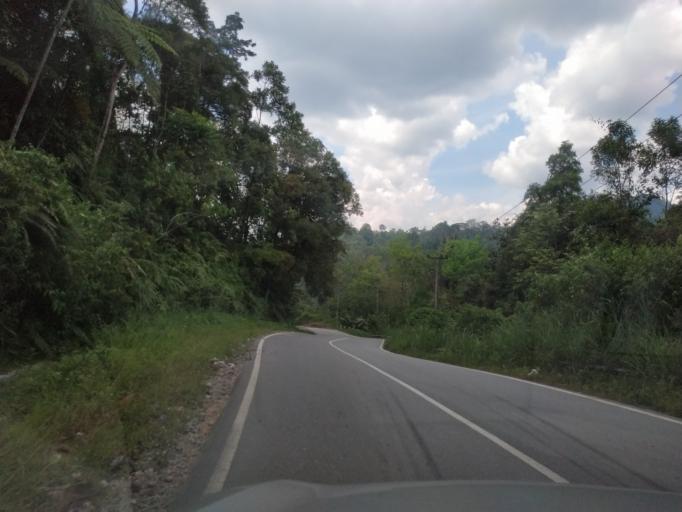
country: ID
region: North Sumatra
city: Sarulla
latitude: 1.8374
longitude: 99.0834
